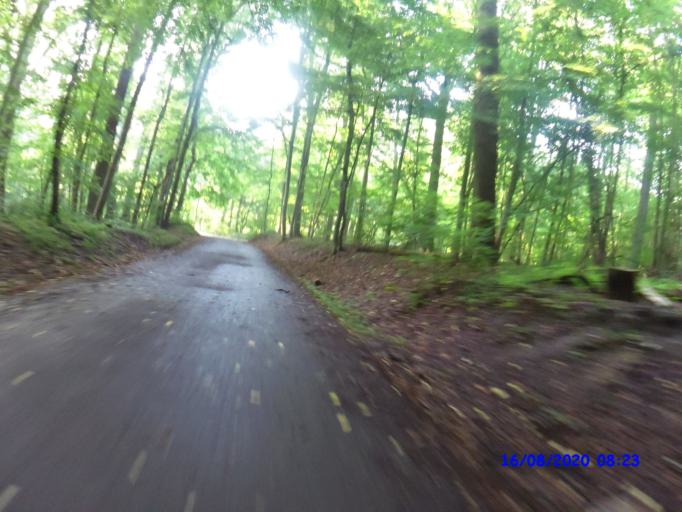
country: BE
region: Flanders
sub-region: Provincie Vlaams-Brabant
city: Sint-Genesius-Rode
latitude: 50.7922
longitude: 4.3997
